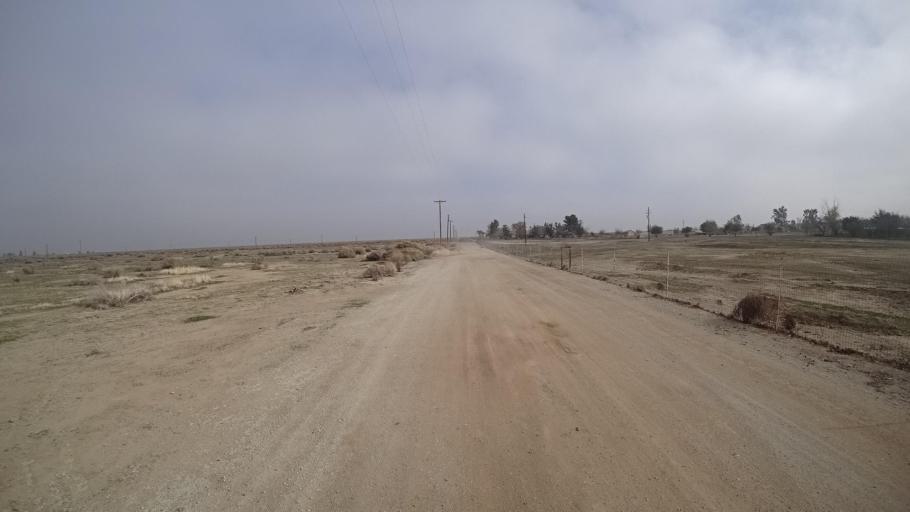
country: US
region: California
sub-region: Kern County
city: Maricopa
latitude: 35.0471
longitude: -119.3564
